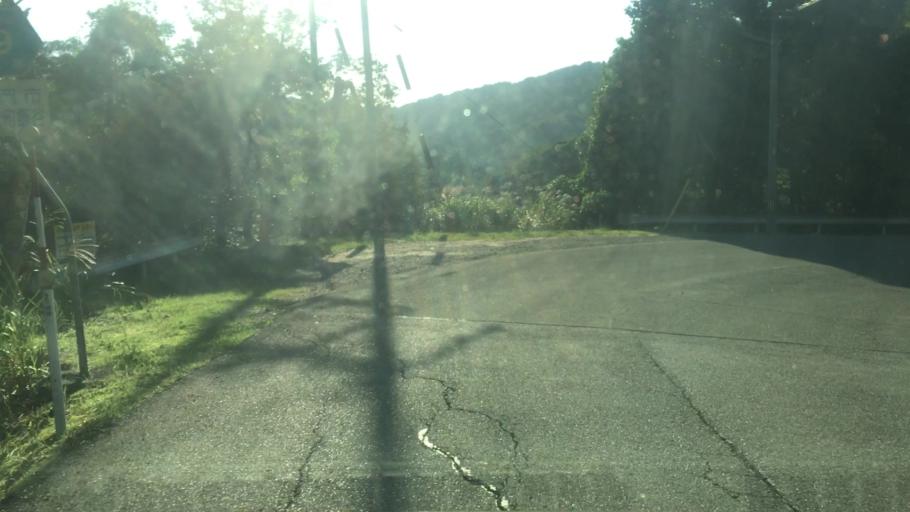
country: JP
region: Hyogo
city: Toyooka
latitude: 35.6106
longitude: 134.8342
